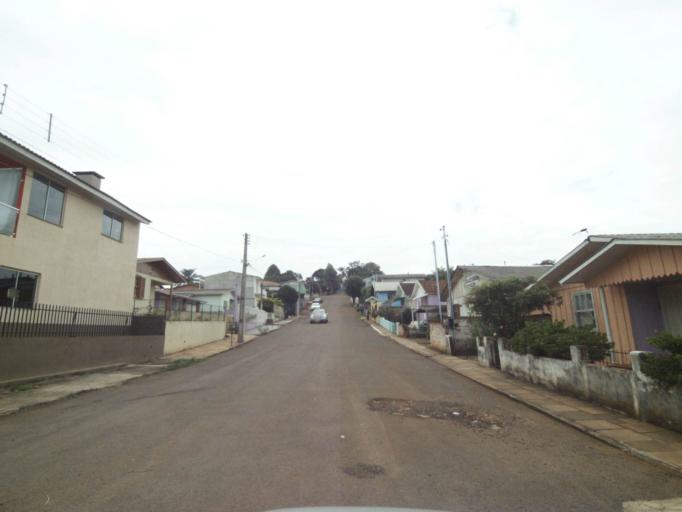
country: BR
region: Rio Grande do Sul
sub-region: Lagoa Vermelha
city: Lagoa Vermelha
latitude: -28.2146
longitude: -51.5357
